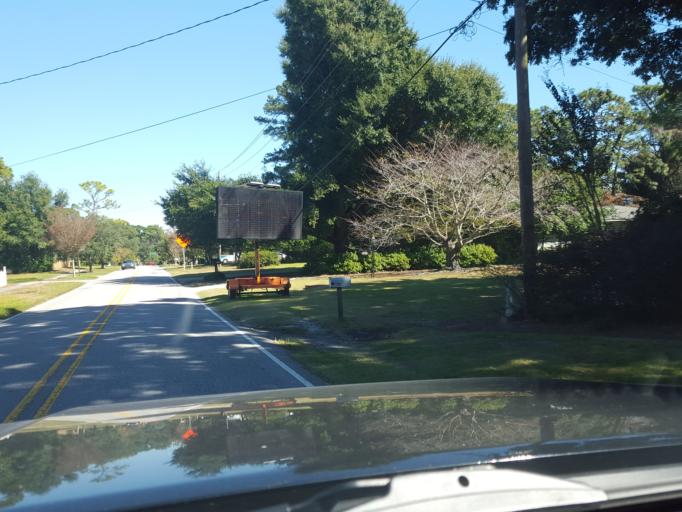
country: US
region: North Carolina
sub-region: New Hanover County
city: Seagate
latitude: 34.2060
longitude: -77.8809
